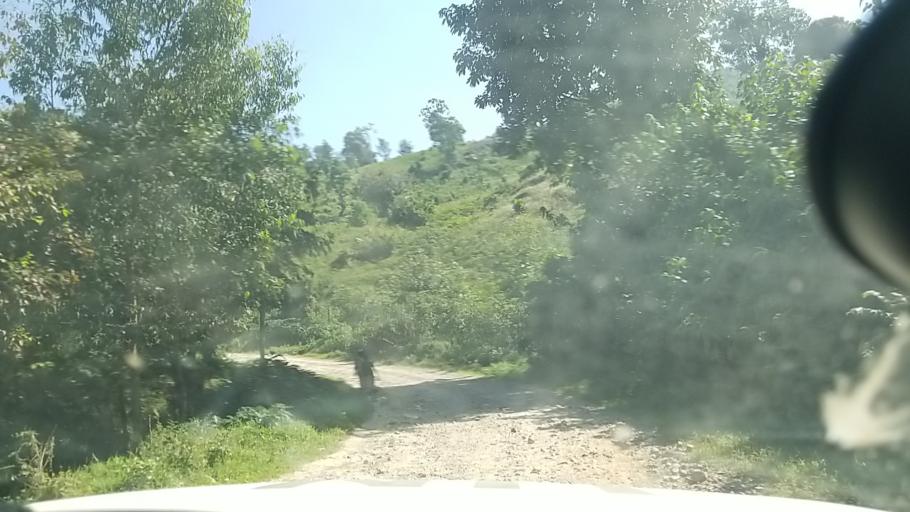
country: CD
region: Nord Kivu
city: Sake
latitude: -1.9890
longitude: 28.9106
